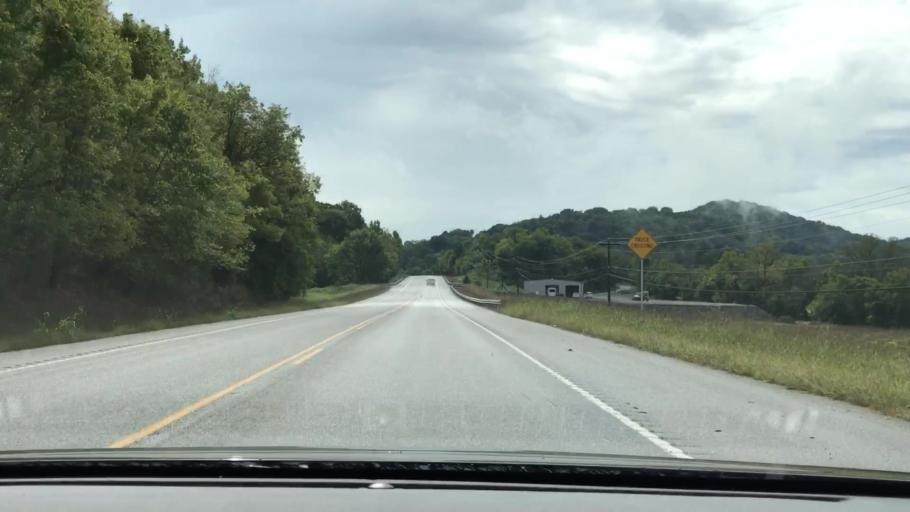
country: US
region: Tennessee
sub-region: Smith County
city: Carthage
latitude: 36.3122
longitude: -85.9717
